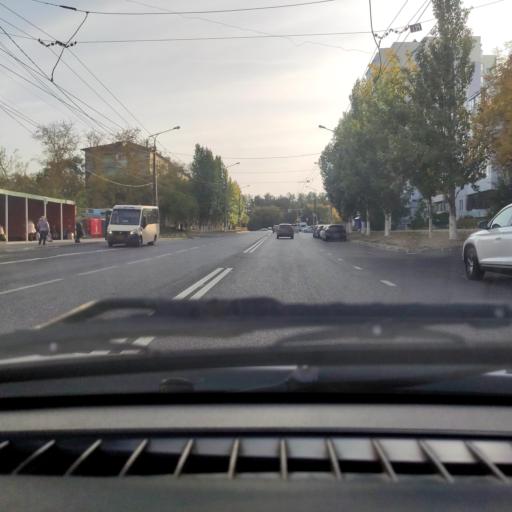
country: RU
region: Samara
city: Zhigulevsk
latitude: 53.4779
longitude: 49.4583
